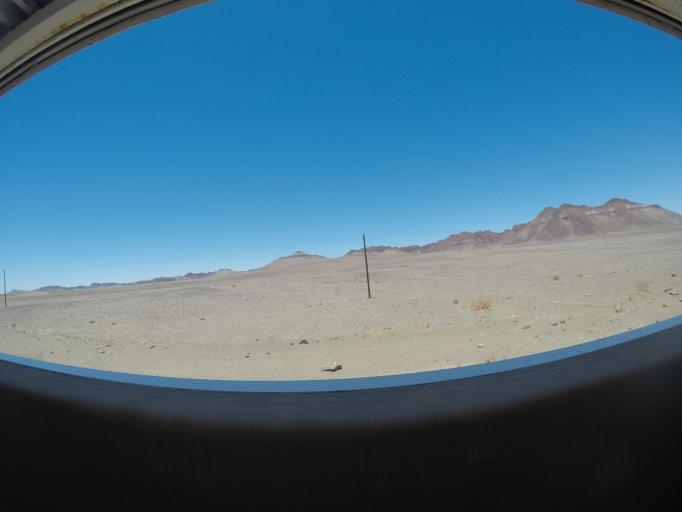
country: ZA
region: Northern Cape
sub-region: Namakwa District Municipality
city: Port Nolloth
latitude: -28.6048
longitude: 17.4868
